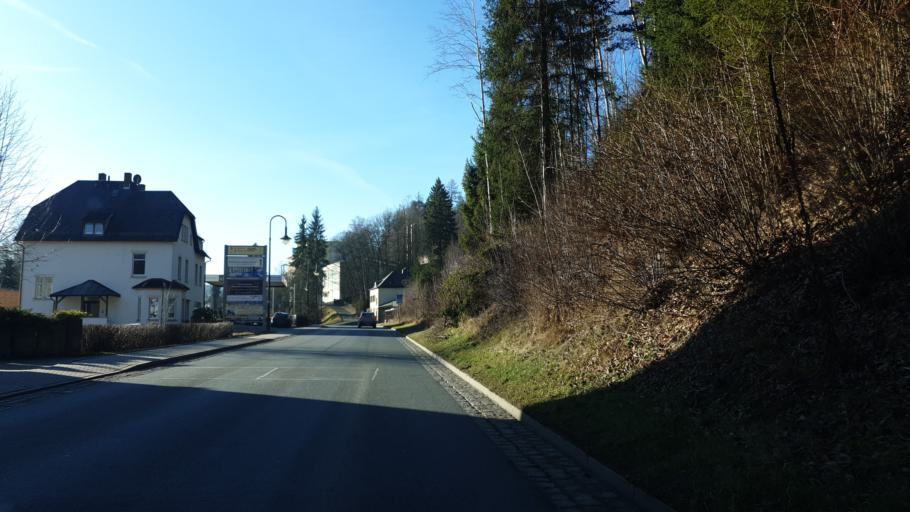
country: DE
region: Saxony
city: Bad Elster
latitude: 50.2901
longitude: 12.2423
